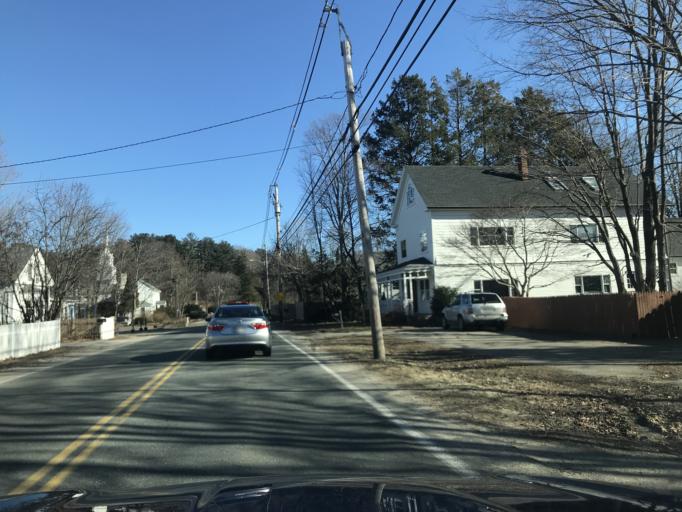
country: US
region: Massachusetts
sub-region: Essex County
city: Groveland
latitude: 42.7069
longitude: -71.0668
